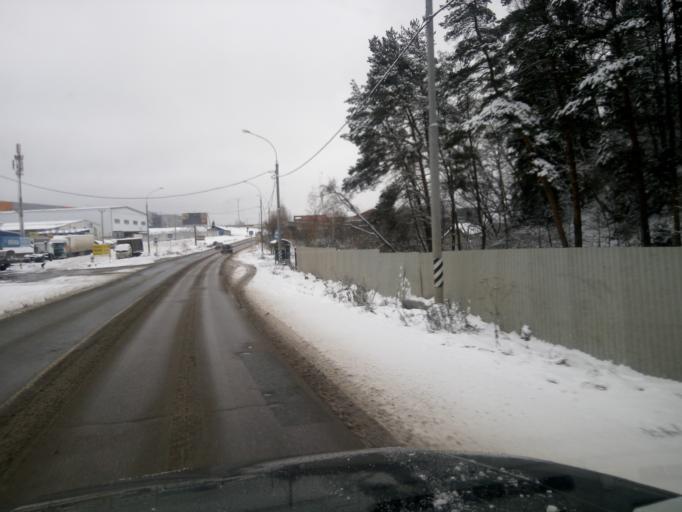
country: RU
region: Moskovskaya
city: Skhodnya
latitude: 55.9677
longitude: 37.3098
